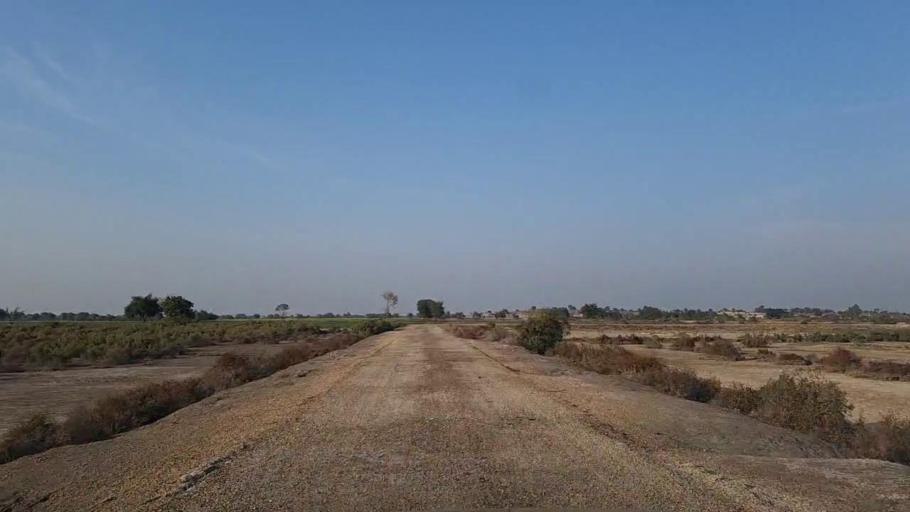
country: PK
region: Sindh
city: Jam Sahib
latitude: 26.3756
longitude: 68.5273
